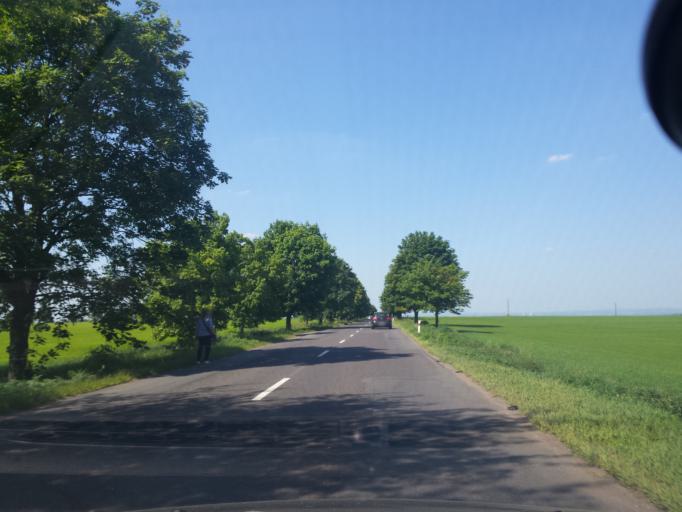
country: CZ
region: Central Bohemia
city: Kralupy nad Vltavou
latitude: 50.2082
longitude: 14.3158
